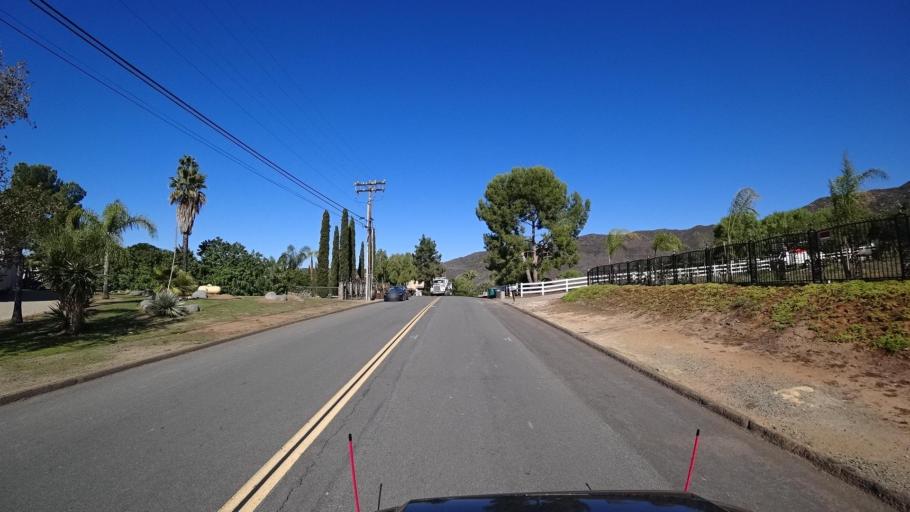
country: US
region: California
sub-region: San Diego County
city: Jamul
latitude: 32.7352
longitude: -116.8544
